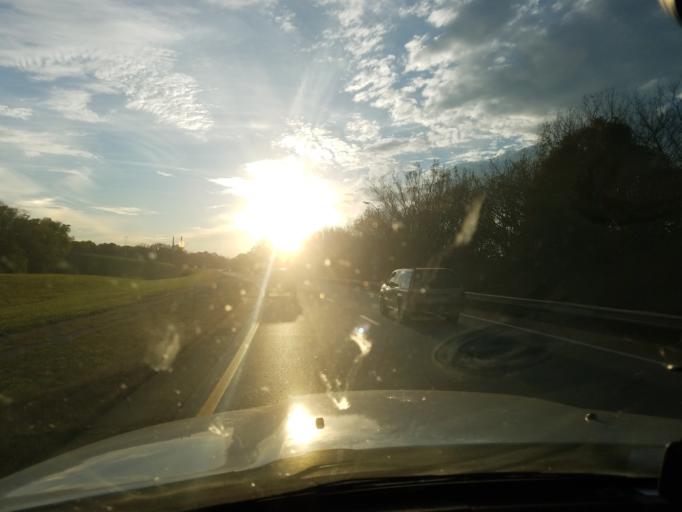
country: US
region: Indiana
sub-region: Floyd County
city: New Albany
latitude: 38.2770
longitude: -85.8089
